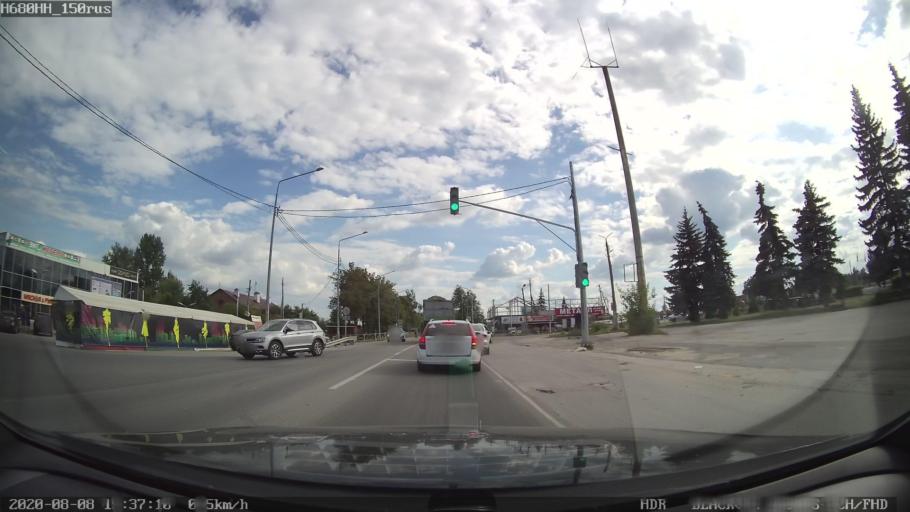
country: RU
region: Tula
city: Zaokskiy
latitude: 54.7478
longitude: 37.4387
